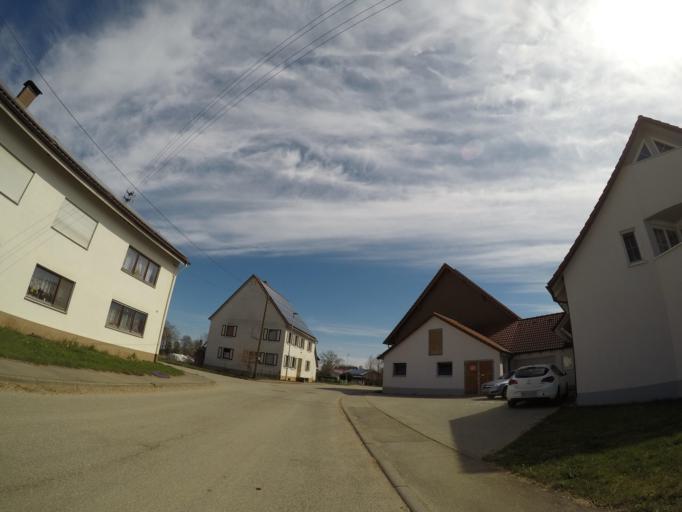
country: DE
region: Baden-Wuerttemberg
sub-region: Tuebingen Region
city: Mehrstetten
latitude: 48.3499
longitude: 9.6100
